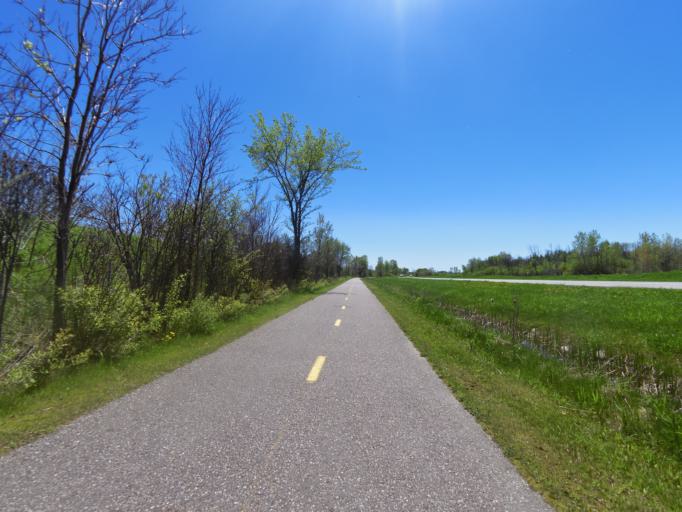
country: CA
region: Ontario
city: Ottawa
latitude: 45.4211
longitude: -75.8005
